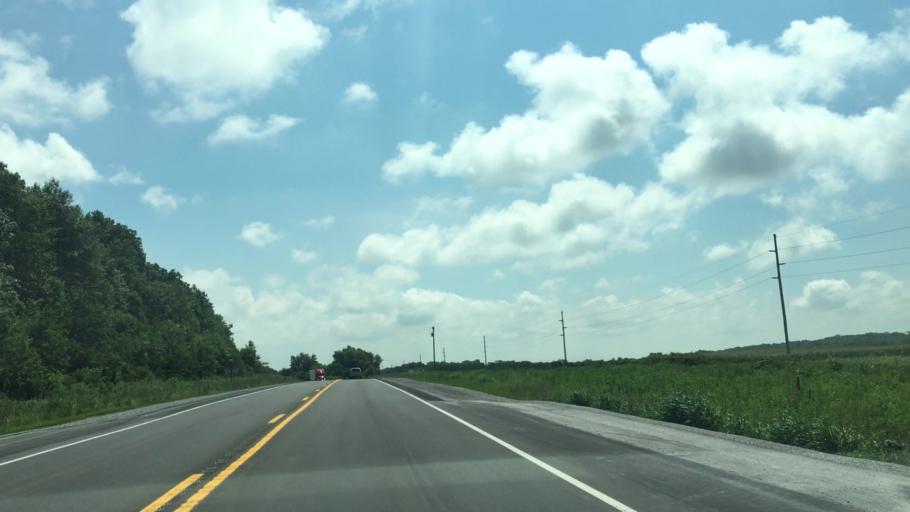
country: US
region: Iowa
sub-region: Johnson County
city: Tiffin
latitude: 41.7175
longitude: -91.7299
